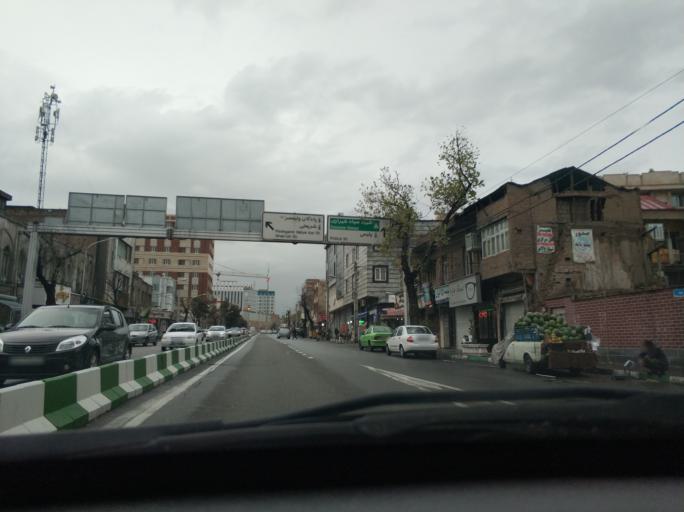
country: IR
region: Tehran
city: Tehran
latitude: 35.7031
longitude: 51.4390
